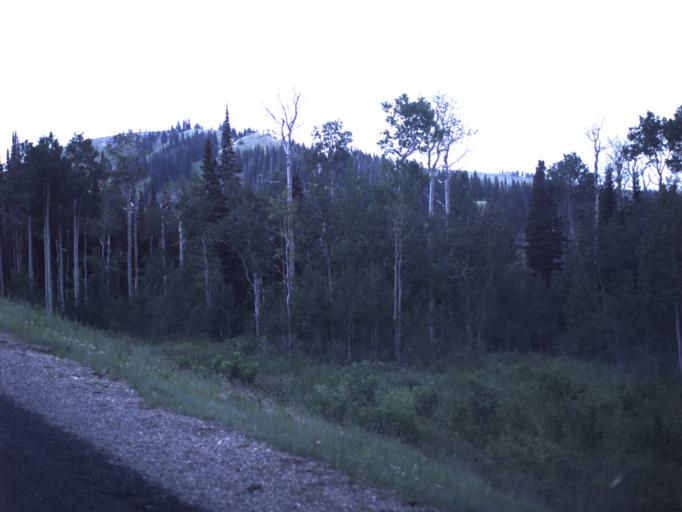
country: US
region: Utah
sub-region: Summit County
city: Francis
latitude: 40.4956
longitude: -111.0348
